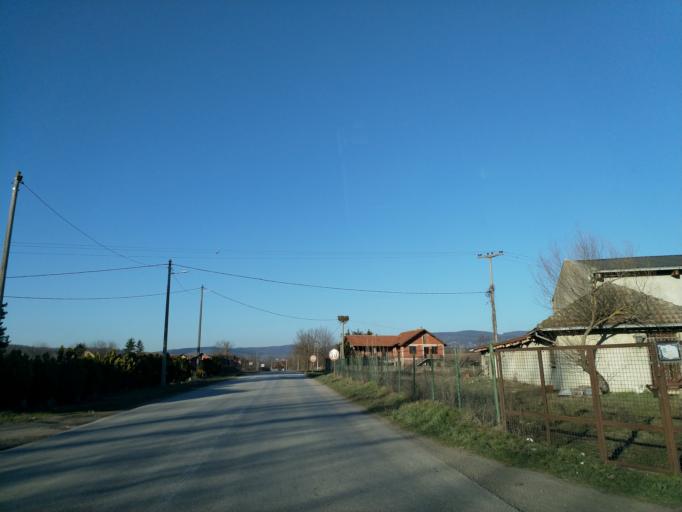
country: RS
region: Central Serbia
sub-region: Pomoravski Okrug
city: Paracin
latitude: 43.8856
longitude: 21.4808
